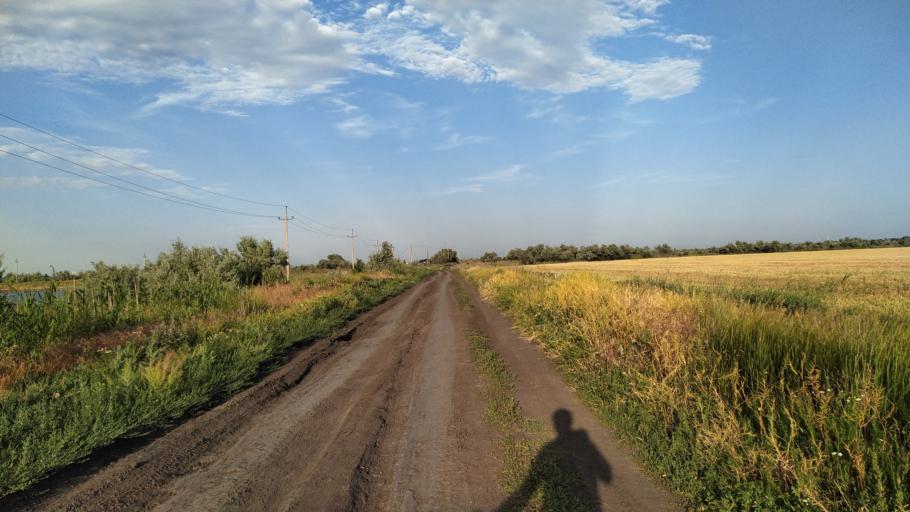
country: RU
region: Rostov
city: Bataysk
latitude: 47.1371
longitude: 39.6532
